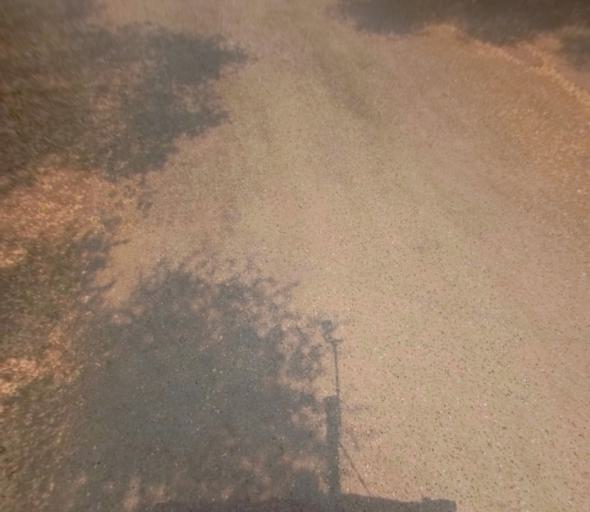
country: US
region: California
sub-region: Madera County
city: Oakhurst
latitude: 37.3211
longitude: -119.6043
